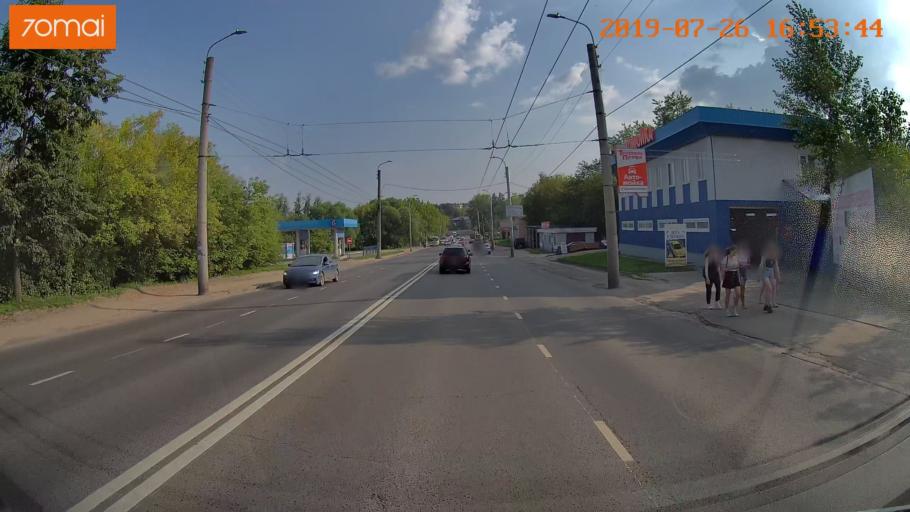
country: RU
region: Ivanovo
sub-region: Gorod Ivanovo
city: Ivanovo
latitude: 57.0133
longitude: 41.0013
